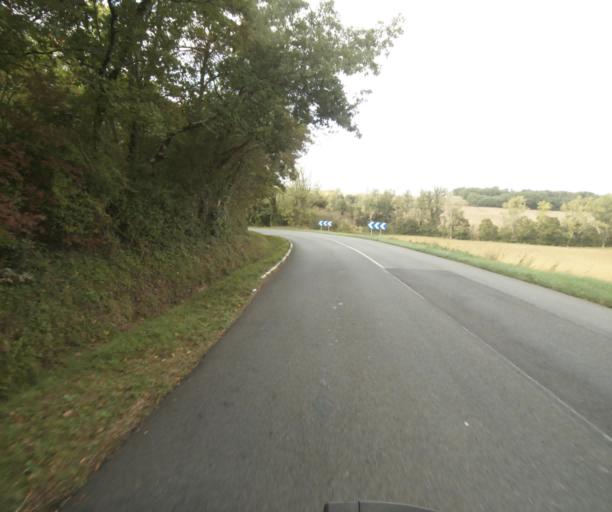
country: FR
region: Midi-Pyrenees
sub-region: Departement du Tarn-et-Garonne
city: Verdun-sur-Garonne
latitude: 43.8531
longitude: 1.1334
